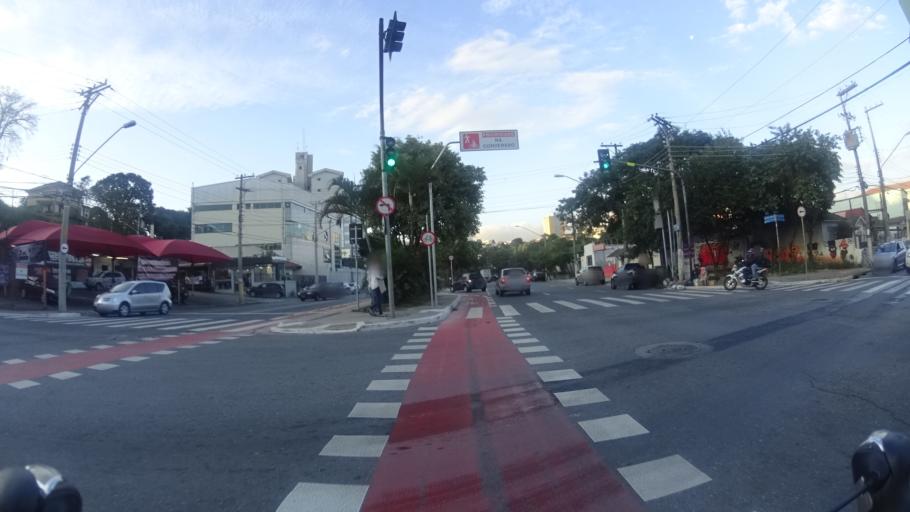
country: BR
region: Sao Paulo
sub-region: Sao Paulo
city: Sao Paulo
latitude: -23.4793
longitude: -46.6282
